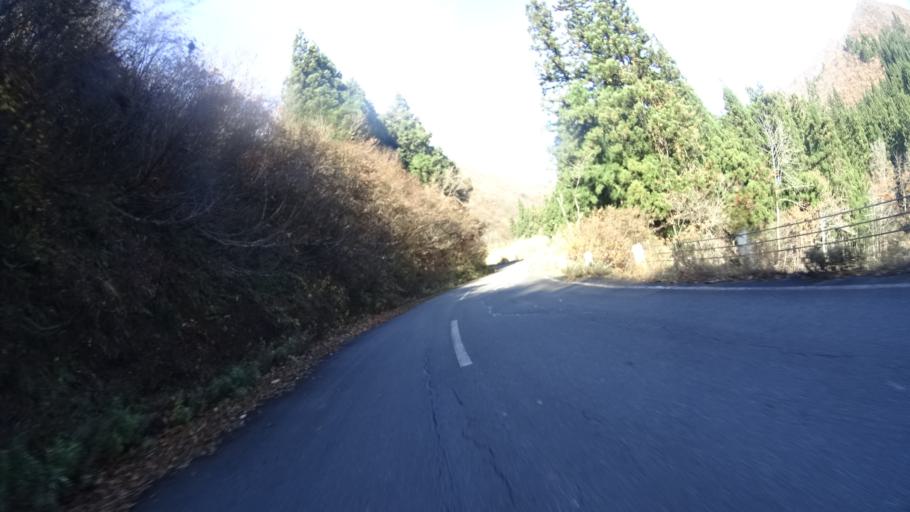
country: JP
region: Niigata
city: Muikamachi
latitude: 37.1813
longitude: 139.0812
